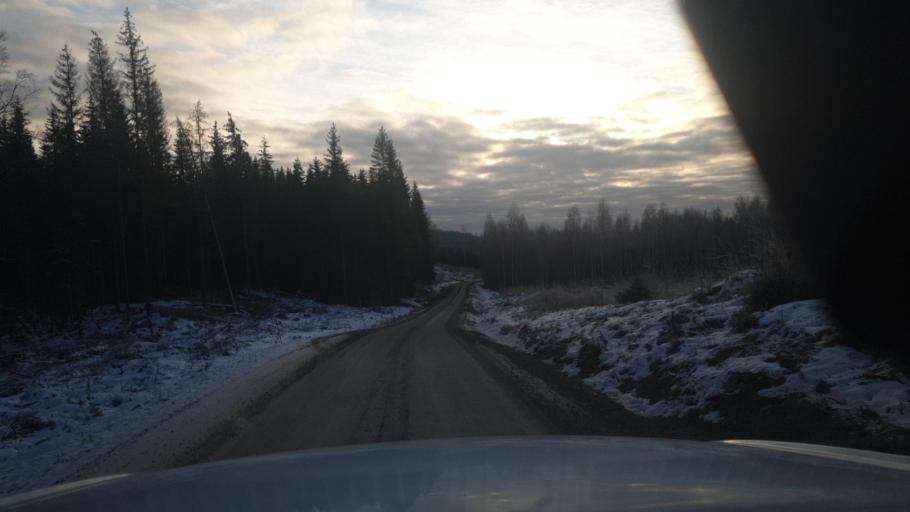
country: SE
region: Vaermland
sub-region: Arvika Kommun
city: Arvika
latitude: 59.9464
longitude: 12.6615
